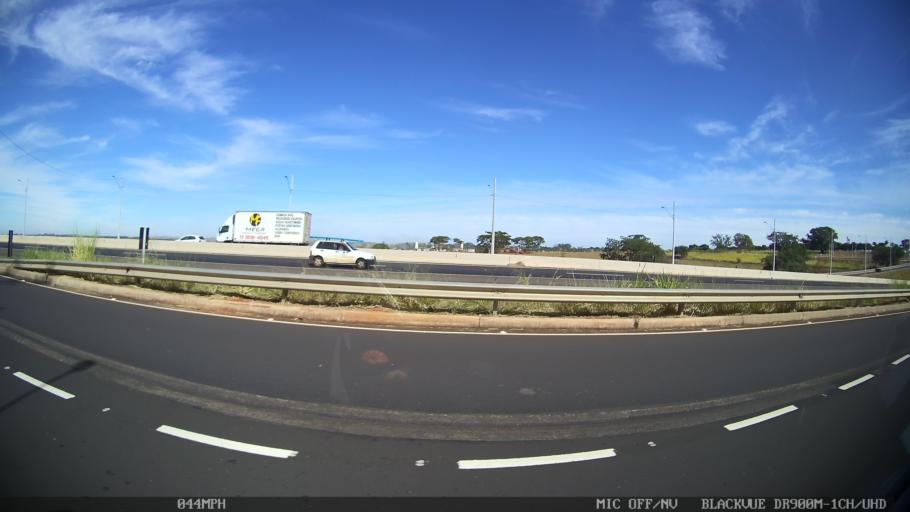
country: BR
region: Sao Paulo
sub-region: Sao Jose Do Rio Preto
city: Sao Jose do Rio Preto
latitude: -20.8502
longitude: -49.3912
